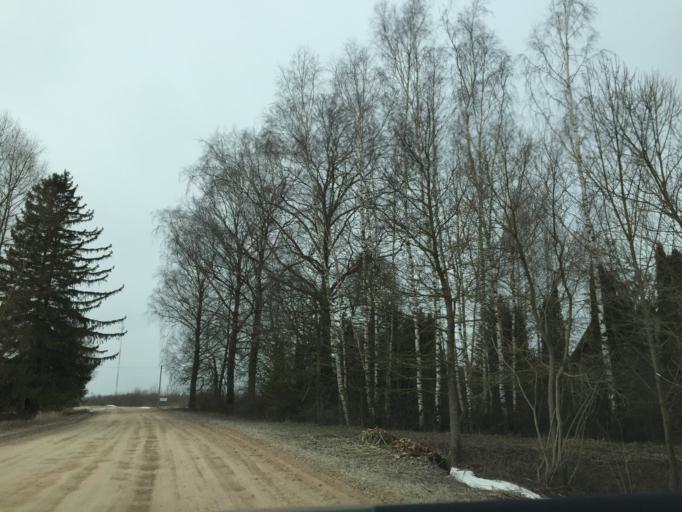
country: LV
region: Rundales
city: Pilsrundale
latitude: 56.5578
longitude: 24.0054
